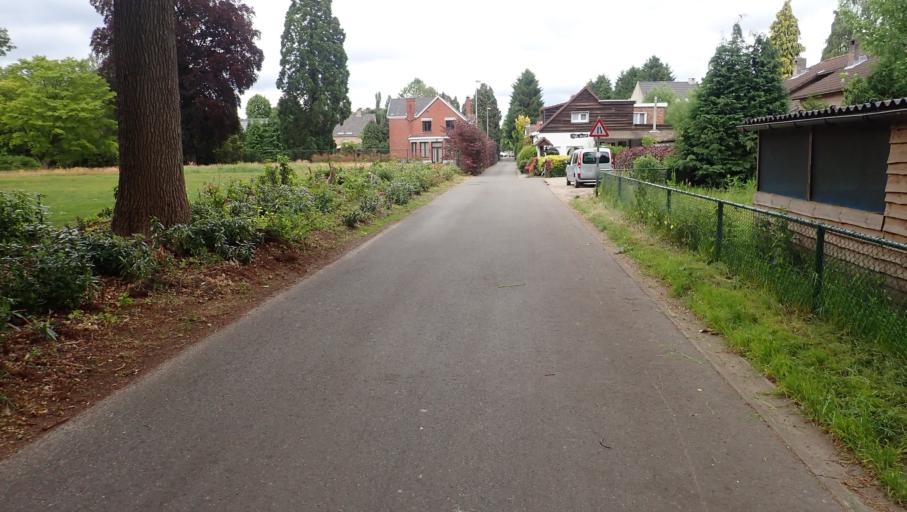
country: BE
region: Flanders
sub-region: Provincie Antwerpen
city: Kalmthout
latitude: 51.3988
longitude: 4.4607
